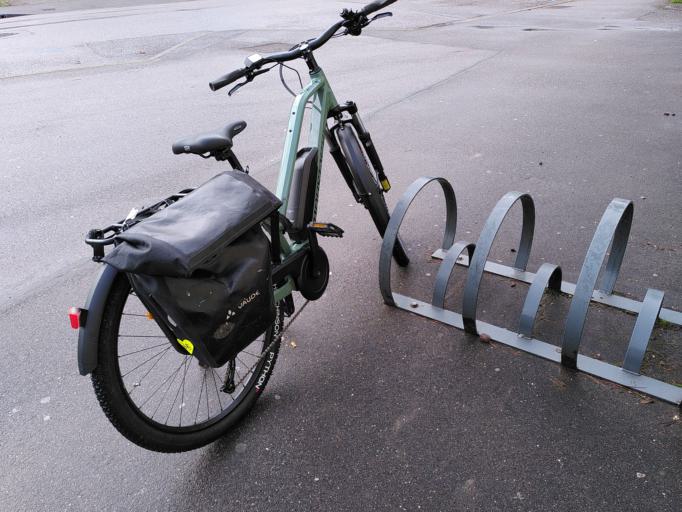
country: FR
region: Lorraine
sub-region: Departement de Meurthe-et-Moselle
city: Frouard
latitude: 48.7550
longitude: 6.1407
